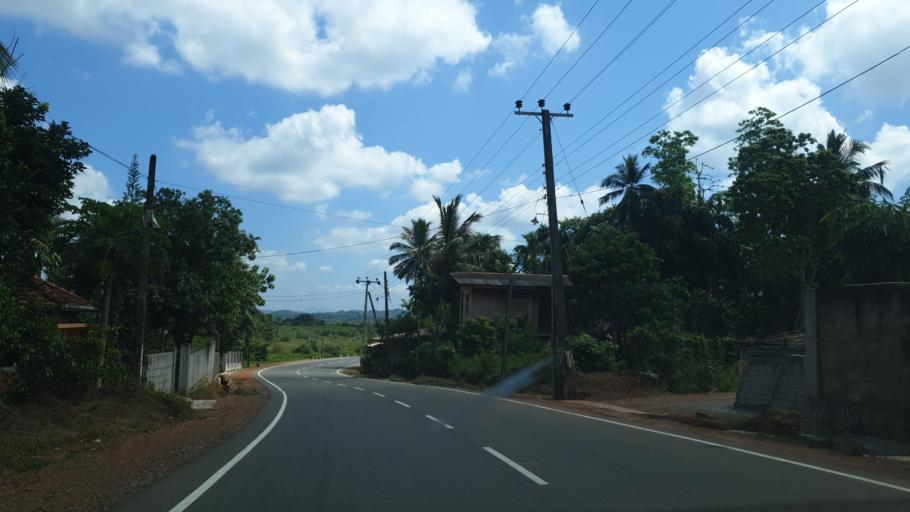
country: LK
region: Western
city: Panadura
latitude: 6.6657
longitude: 79.9662
